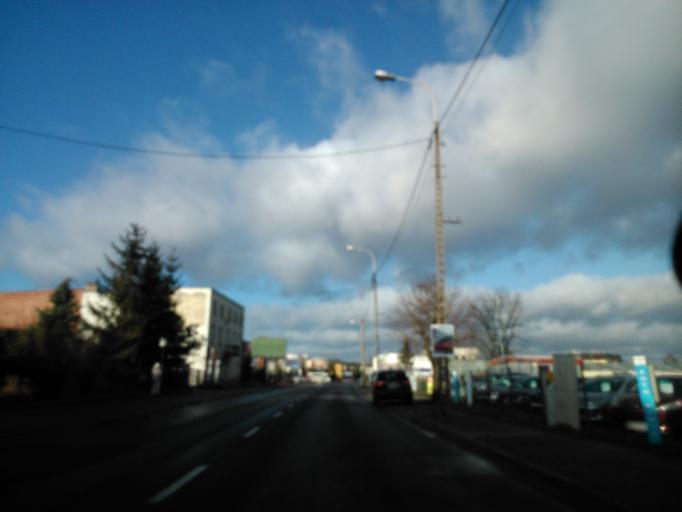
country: PL
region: Kujawsko-Pomorskie
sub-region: Torun
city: Torun
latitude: 52.9954
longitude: 18.6265
